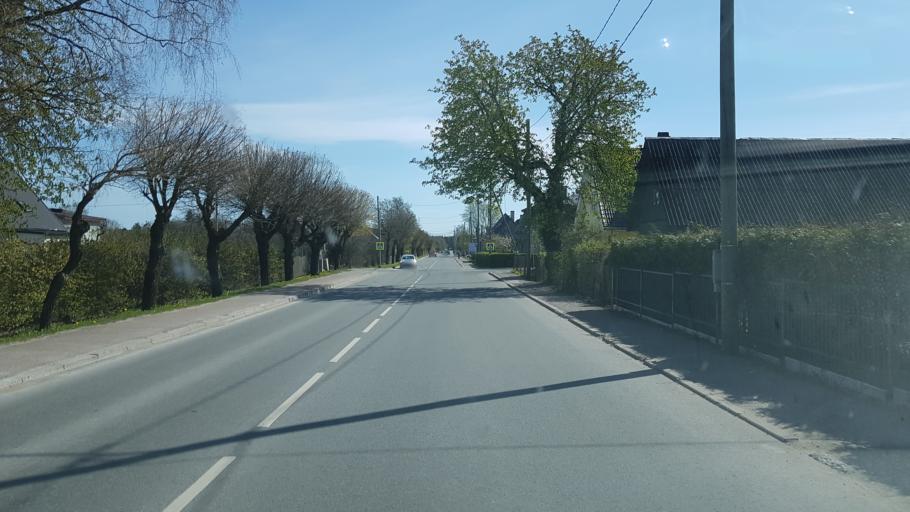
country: EE
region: Harju
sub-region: Keila linn
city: Keila
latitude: 59.3058
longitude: 24.4254
